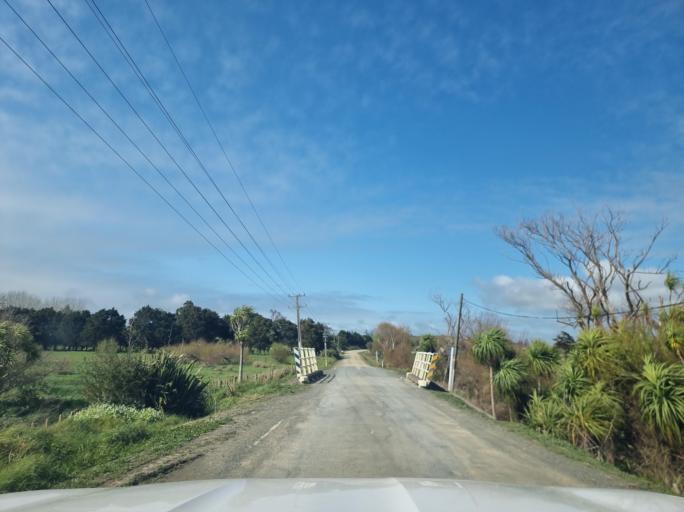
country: NZ
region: Auckland
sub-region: Auckland
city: Wellsford
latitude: -36.1249
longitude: 174.5002
